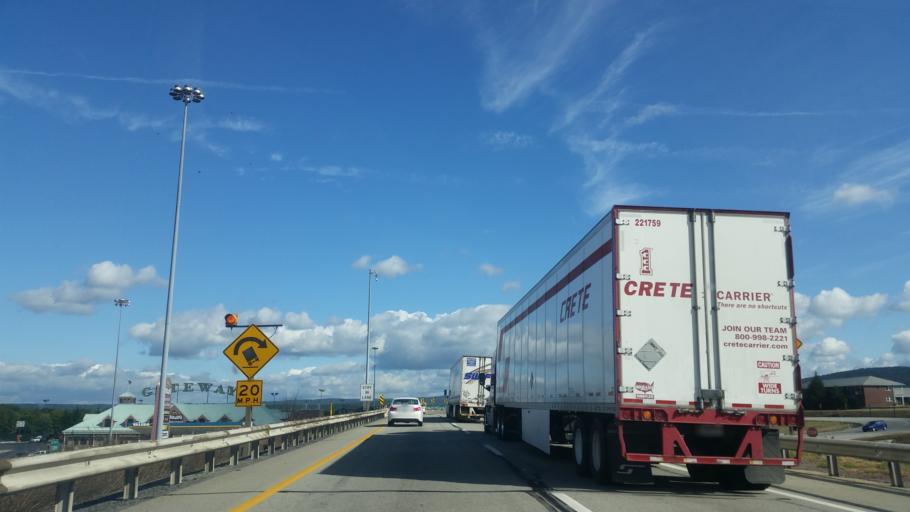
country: US
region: Pennsylvania
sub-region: Bedford County
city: Earlston
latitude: 39.9985
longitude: -78.2332
